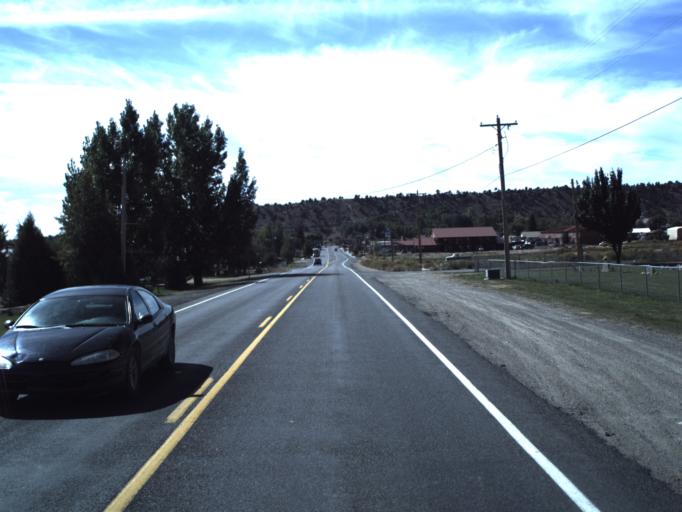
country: US
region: Utah
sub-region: Garfield County
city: Panguitch
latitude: 37.6298
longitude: -112.0819
